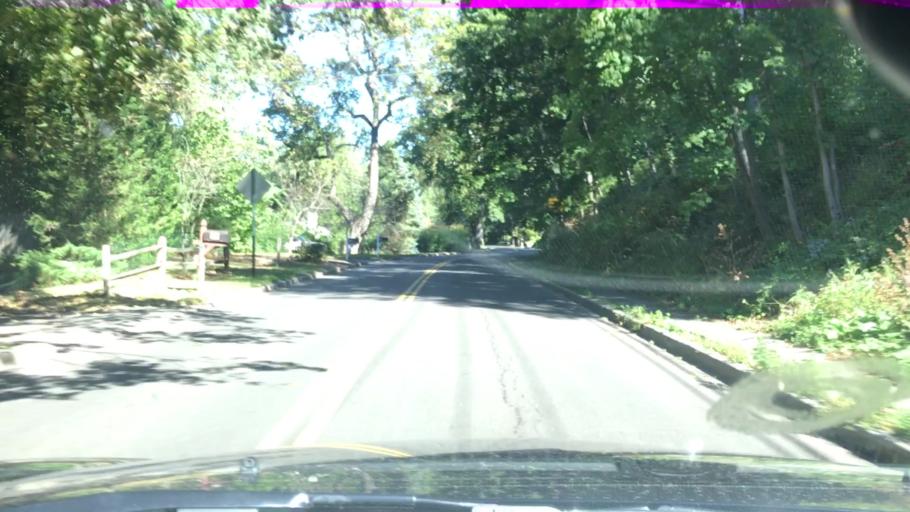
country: US
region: Connecticut
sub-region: Fairfield County
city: Darien
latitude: 41.0835
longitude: -73.4408
